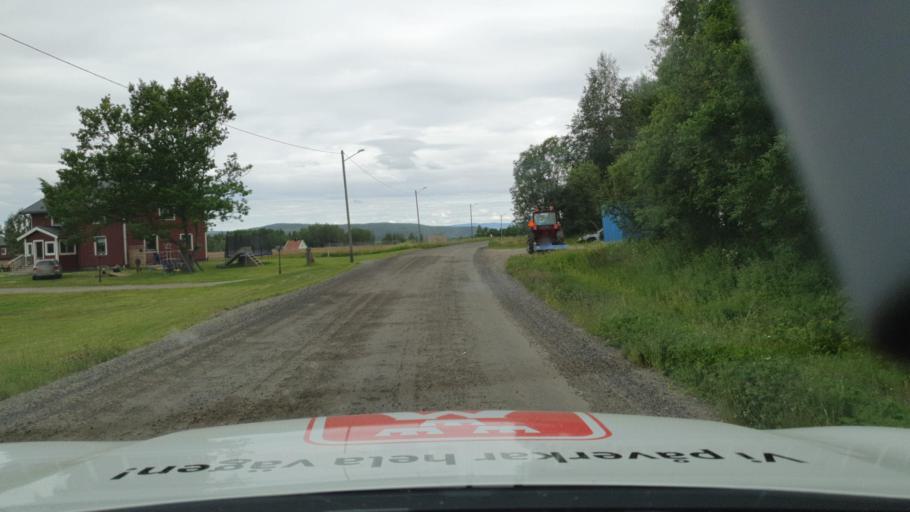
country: SE
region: Vaesterbotten
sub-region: Bjurholms Kommun
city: Bjurholm
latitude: 63.7819
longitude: 19.3813
